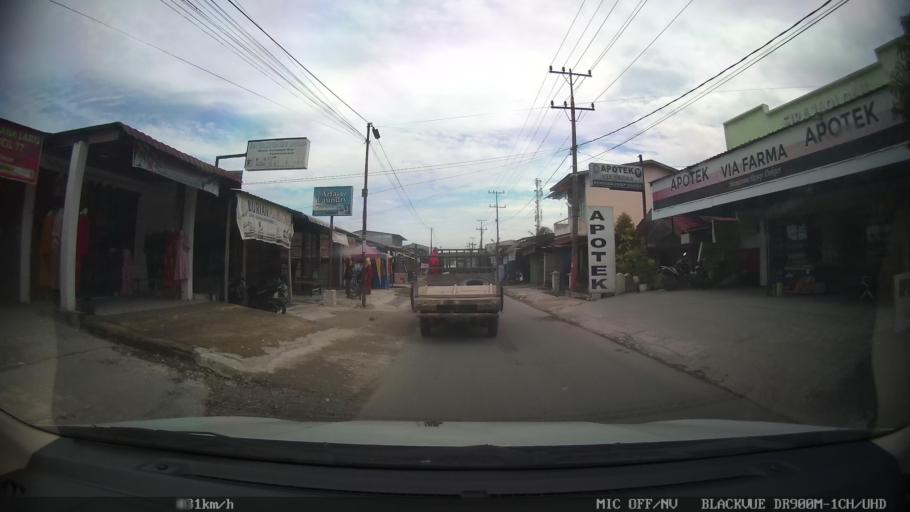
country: ID
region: North Sumatra
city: Sunggal
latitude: 3.6060
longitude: 98.5806
